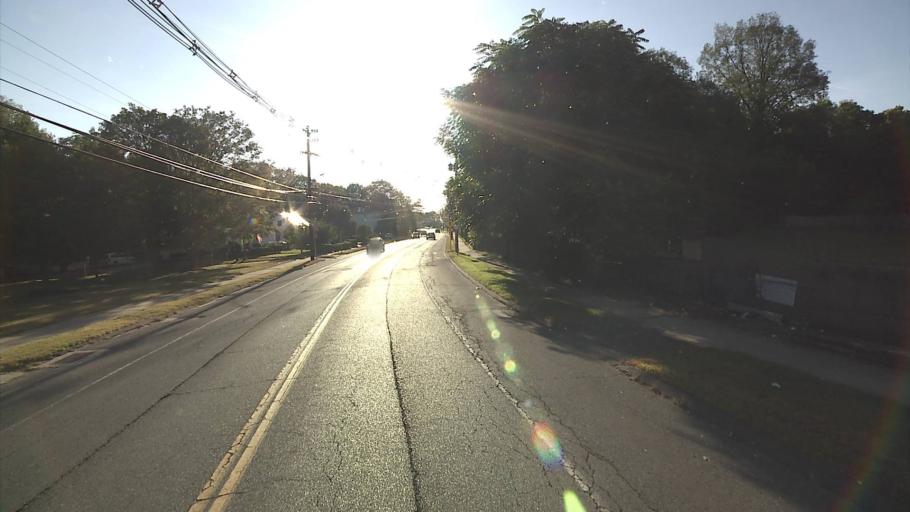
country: US
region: Connecticut
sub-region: Windham County
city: Willimantic
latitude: 41.7097
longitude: -72.2142
